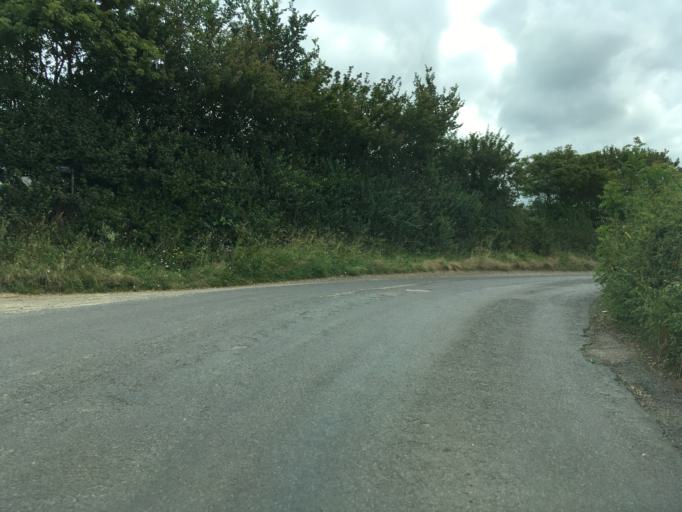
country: GB
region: England
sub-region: Oxfordshire
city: Charlbury
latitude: 51.8959
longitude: -1.4977
